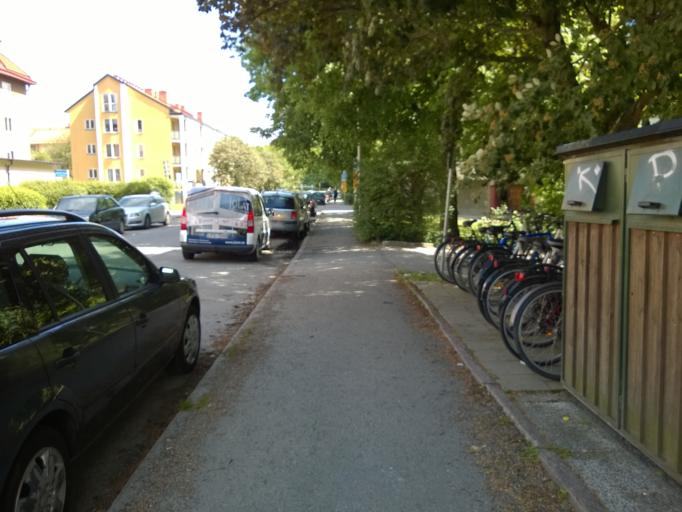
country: SE
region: Stockholm
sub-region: Solna Kommun
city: Rasunda
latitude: 59.3605
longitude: 17.9902
